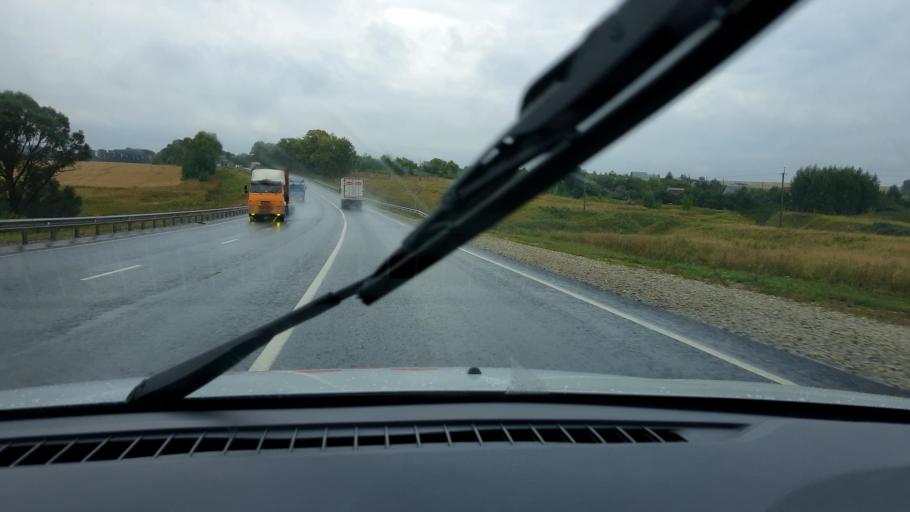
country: RU
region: Chuvashia
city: Tsivil'sk
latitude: 55.7908
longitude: 47.6760
